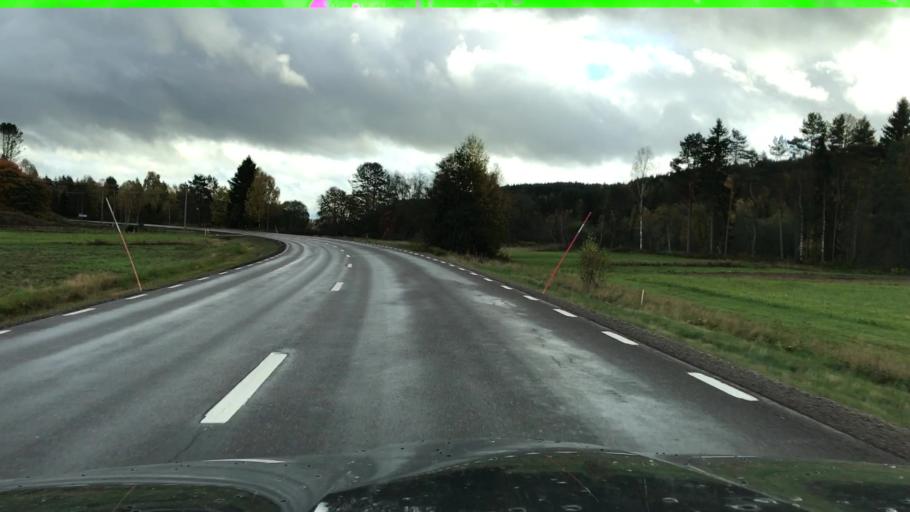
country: SE
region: Vaermland
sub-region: Hagfors Kommun
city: Ekshaerad
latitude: 60.4323
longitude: 13.2384
